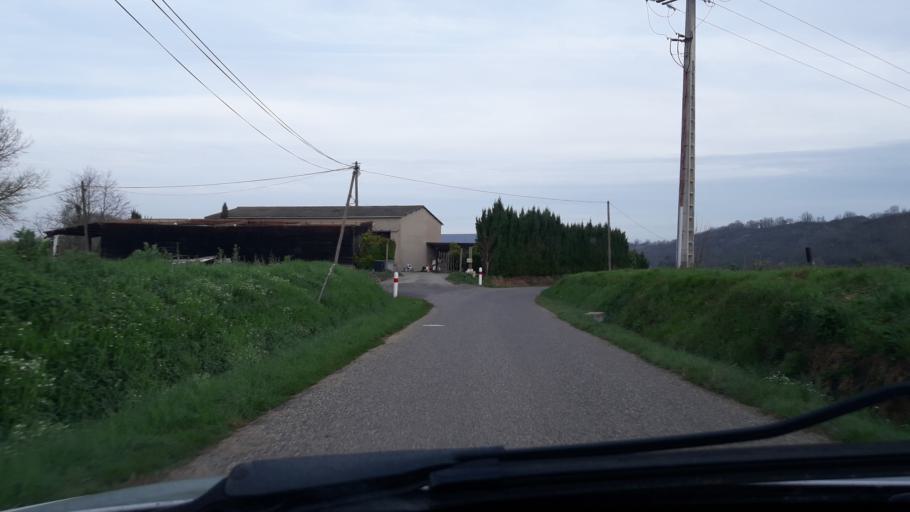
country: FR
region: Midi-Pyrenees
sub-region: Departement de la Haute-Garonne
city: Montesquieu-Volvestre
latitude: 43.1731
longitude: 1.2695
